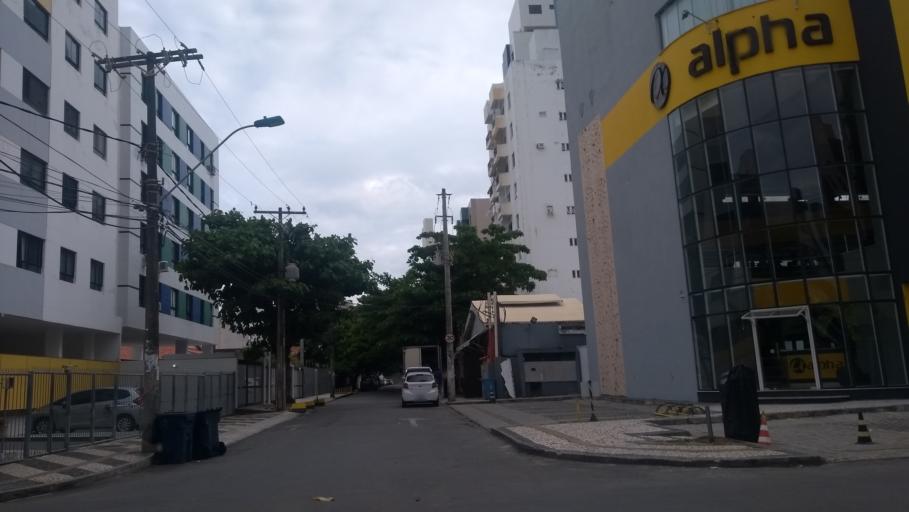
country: BR
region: Bahia
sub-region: Salvador
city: Salvador
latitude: -12.9937
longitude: -38.4468
